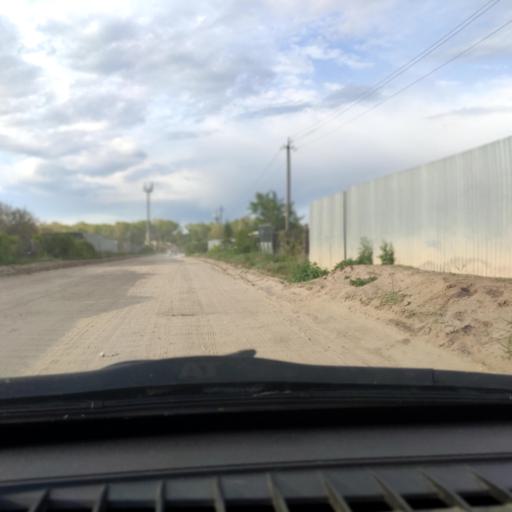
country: RU
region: Samara
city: Zhigulevsk
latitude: 53.4539
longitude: 49.5351
